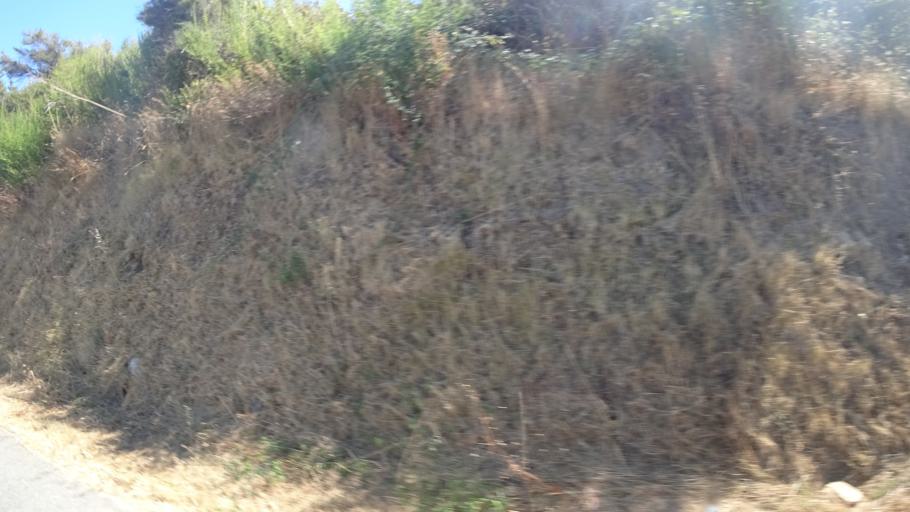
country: FR
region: Corsica
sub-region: Departement de la Corse-du-Sud
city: Alata
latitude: 41.9702
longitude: 8.6975
